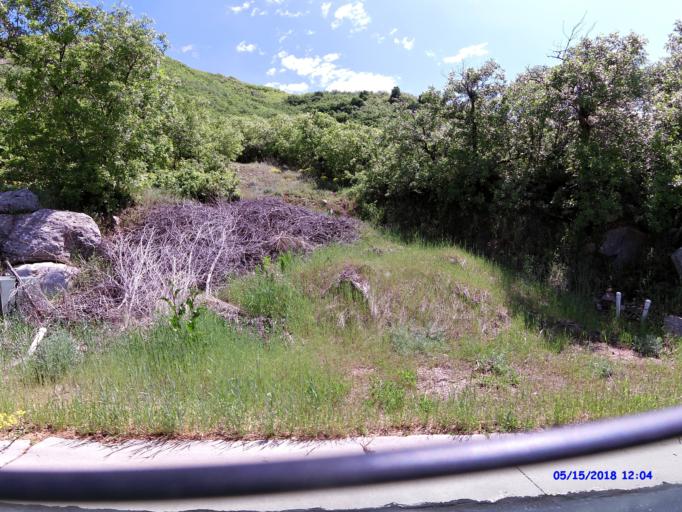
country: US
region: Utah
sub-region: Weber County
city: Uintah
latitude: 41.1825
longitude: -111.9310
